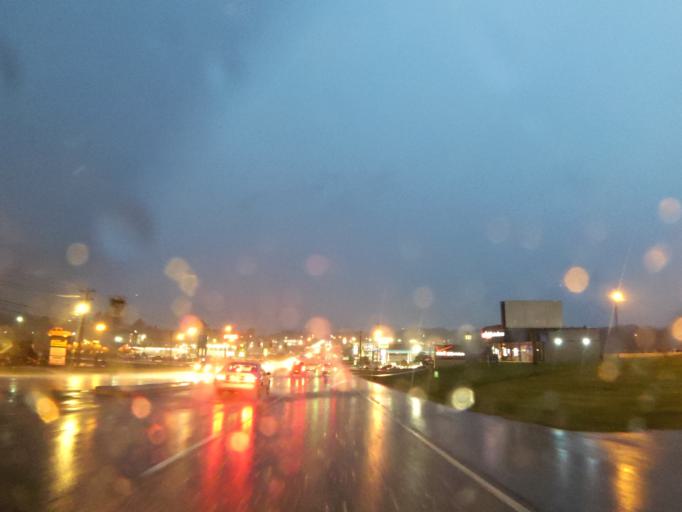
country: US
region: Tennessee
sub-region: Loudon County
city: Lenoir City
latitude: 35.8258
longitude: -84.2750
